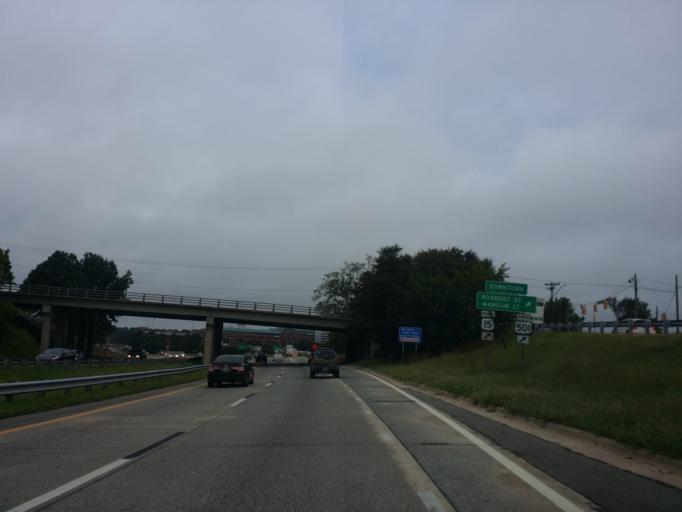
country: US
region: North Carolina
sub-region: Durham County
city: Durham
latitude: 35.9872
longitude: -78.8963
